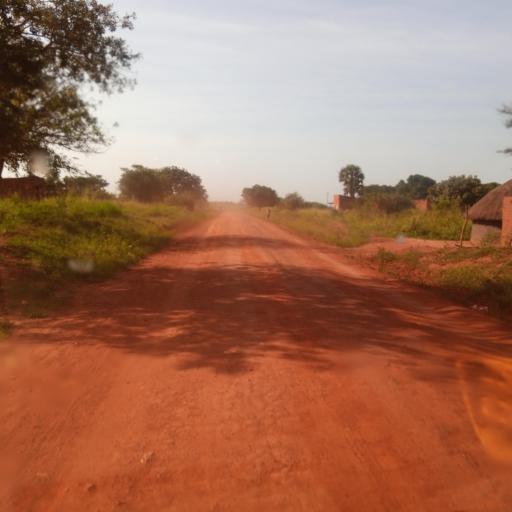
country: UG
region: Northern Region
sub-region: Kitgum District
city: Kitgum
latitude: 3.1094
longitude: 32.9144
